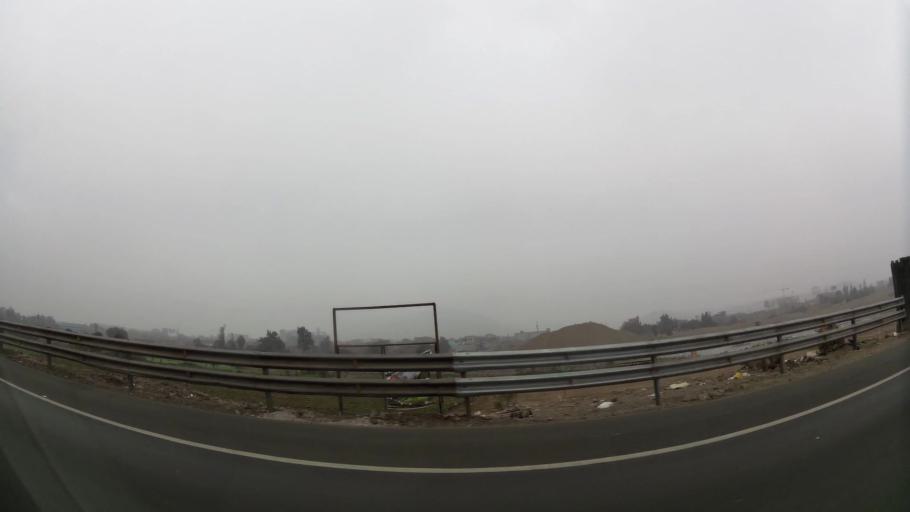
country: PE
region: Lima
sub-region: Lima
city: Santa Maria
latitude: -12.0167
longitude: -76.9079
